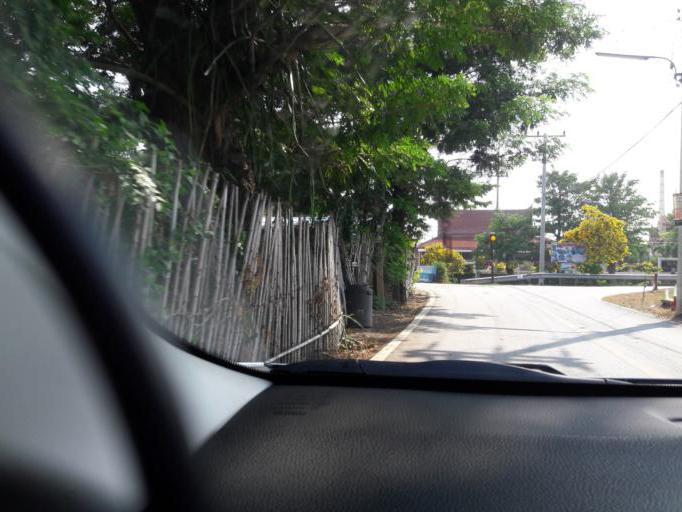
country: TH
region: Ang Thong
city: Pa Mok
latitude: 14.5315
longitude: 100.3929
